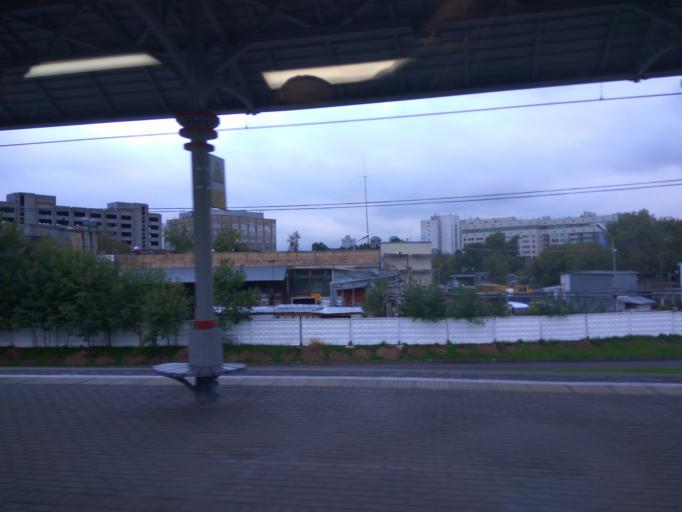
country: RU
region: Moscow
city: Pokrovskoye-Streshnevo
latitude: 55.8135
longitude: 37.4871
